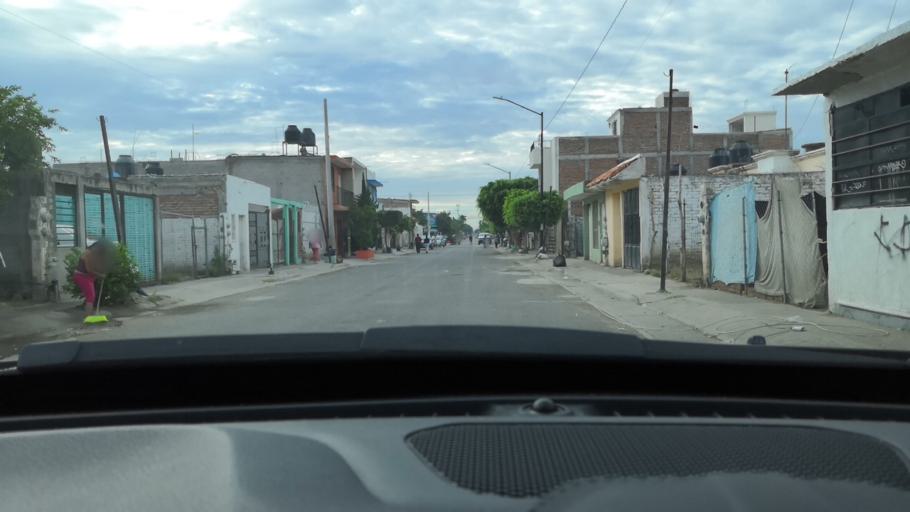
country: MX
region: Guanajuato
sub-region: Leon
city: Fraccionamiento Paraiso Real
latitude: 21.0999
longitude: -101.5891
